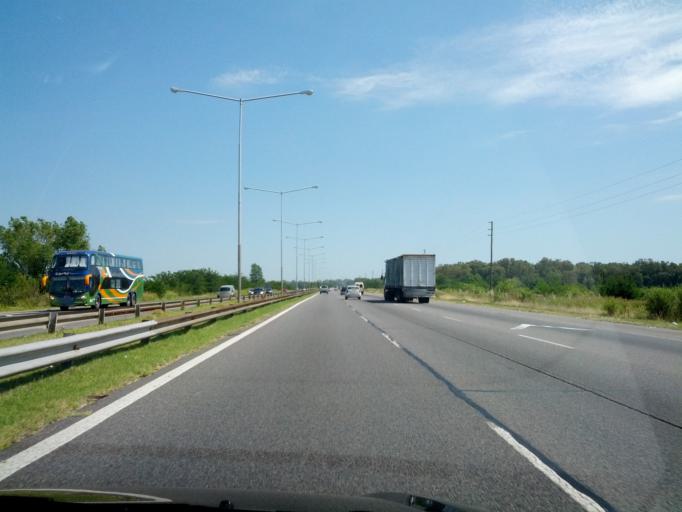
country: AR
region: Buenos Aires
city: Belen de Escobar
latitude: -34.3028
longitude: -58.8786
